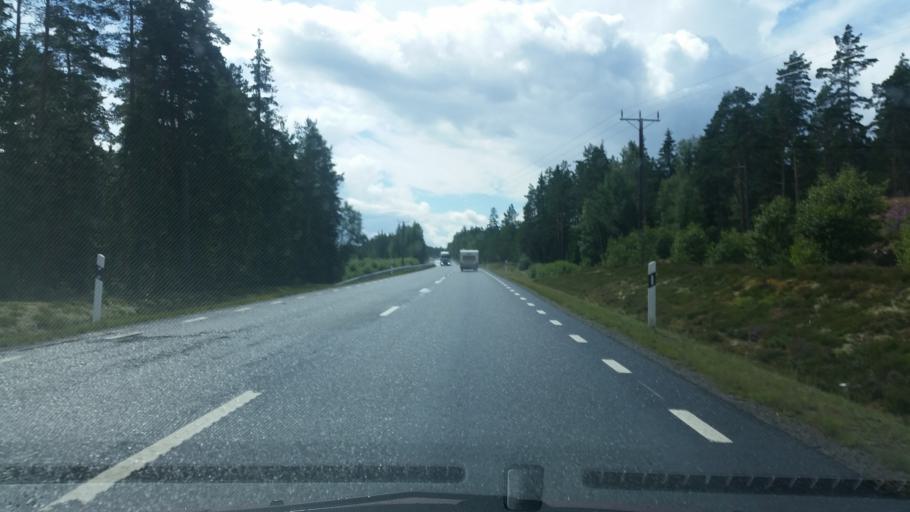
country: SE
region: Joenkoeping
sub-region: Gislaveds Kommun
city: Gislaved
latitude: 57.3968
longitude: 13.5931
